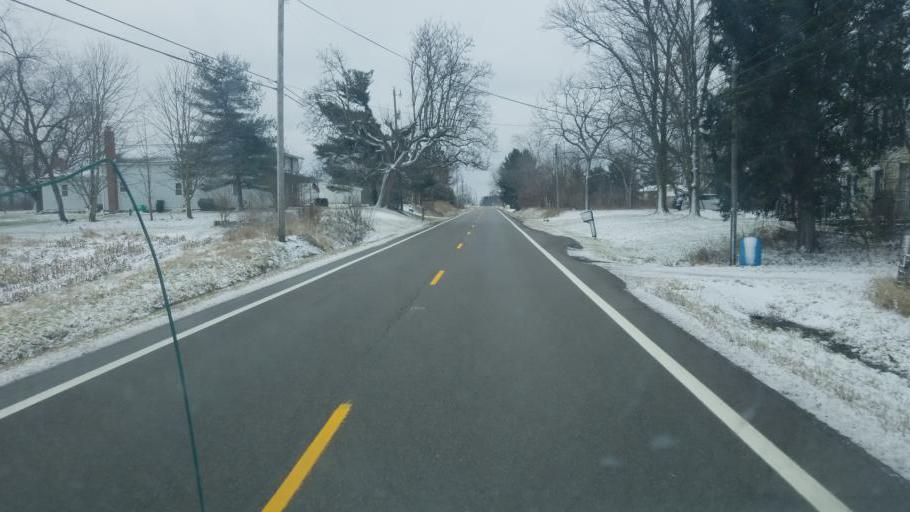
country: US
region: Ohio
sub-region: Licking County
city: Johnstown
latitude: 40.1766
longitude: -82.7307
